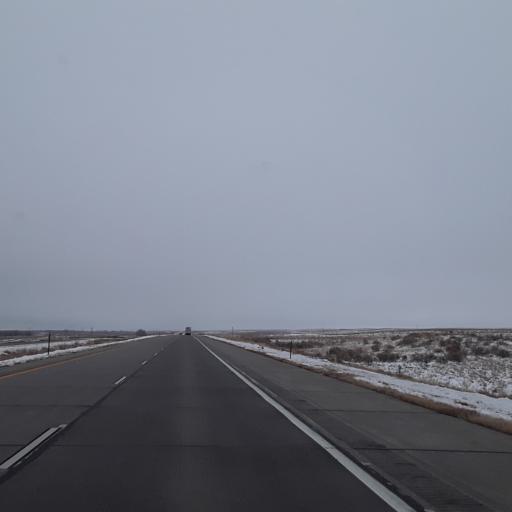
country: US
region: Colorado
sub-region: Logan County
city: Sterling
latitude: 40.5598
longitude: -103.2115
